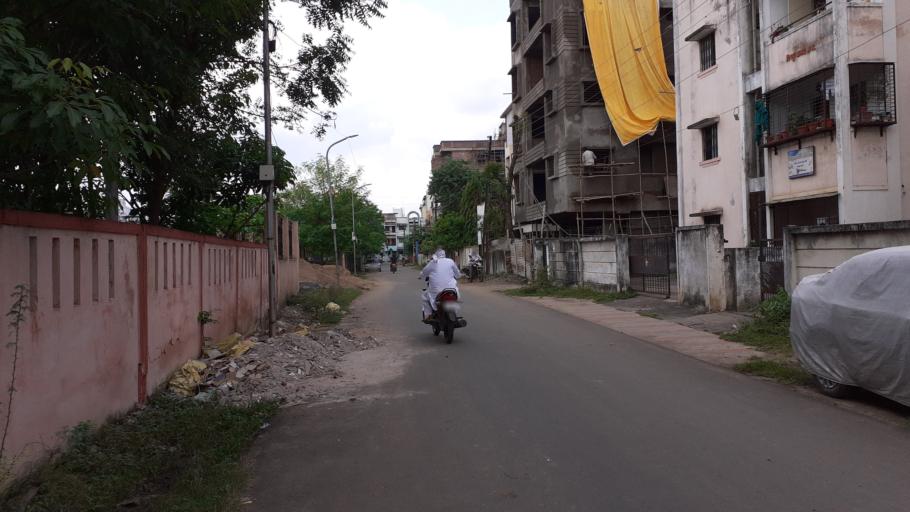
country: IN
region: Maharashtra
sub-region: Nagpur Division
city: Nagpur
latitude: 21.1380
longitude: 79.1220
